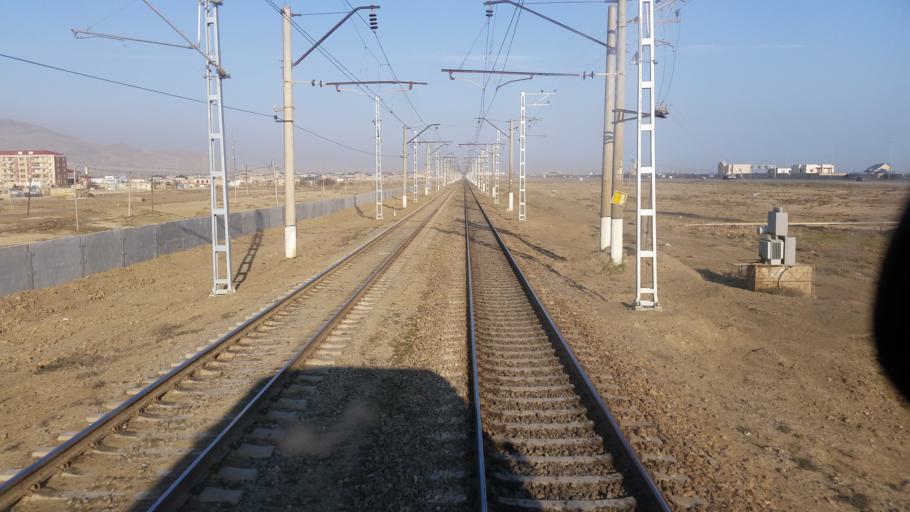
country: AZ
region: Baki
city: Qobustan
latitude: 40.1946
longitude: 49.5043
